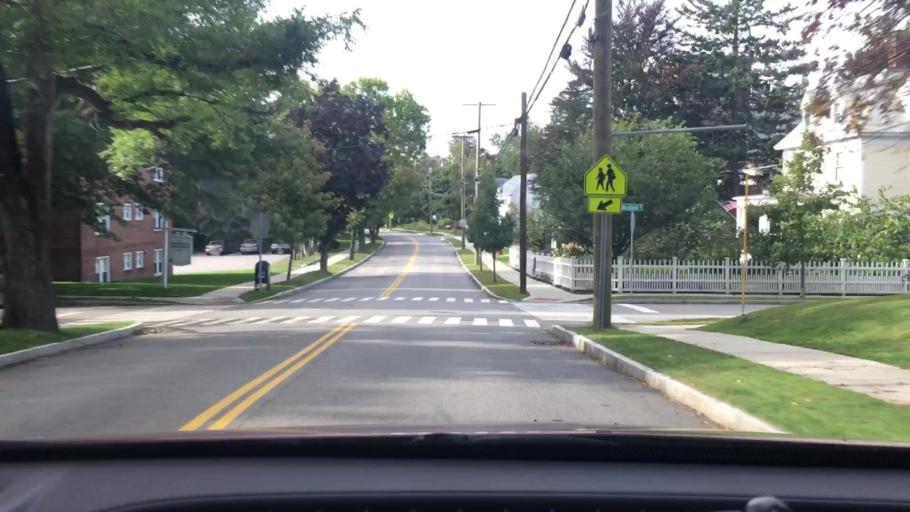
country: US
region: New Hampshire
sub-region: Rockingham County
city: Portsmouth
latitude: 43.0701
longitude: -70.7607
